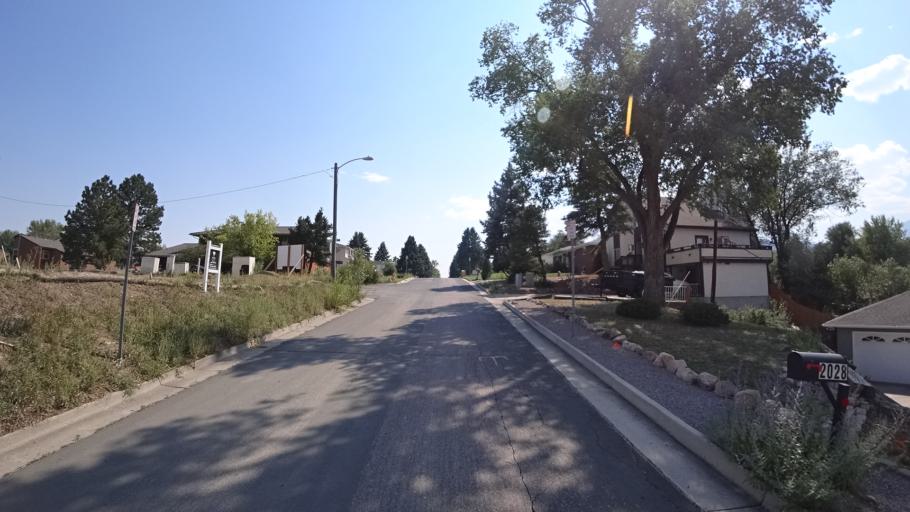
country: US
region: Colorado
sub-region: El Paso County
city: Colorado Springs
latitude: 38.8031
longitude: -104.8282
